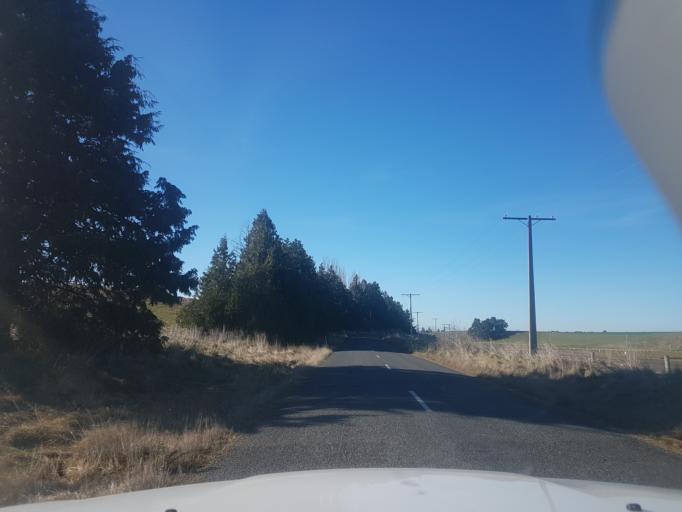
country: NZ
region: Canterbury
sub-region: Timaru District
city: Pleasant Point
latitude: -44.2730
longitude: 171.1273
